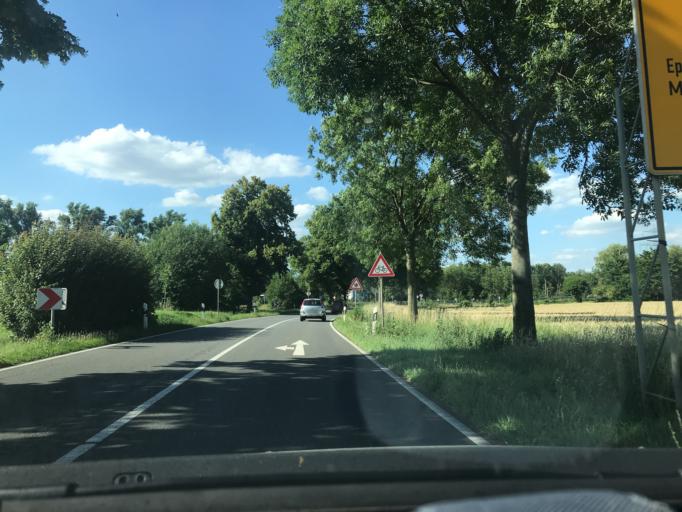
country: DE
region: North Rhine-Westphalia
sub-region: Regierungsbezirk Dusseldorf
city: Neubrueck
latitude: 51.1511
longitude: 6.6791
